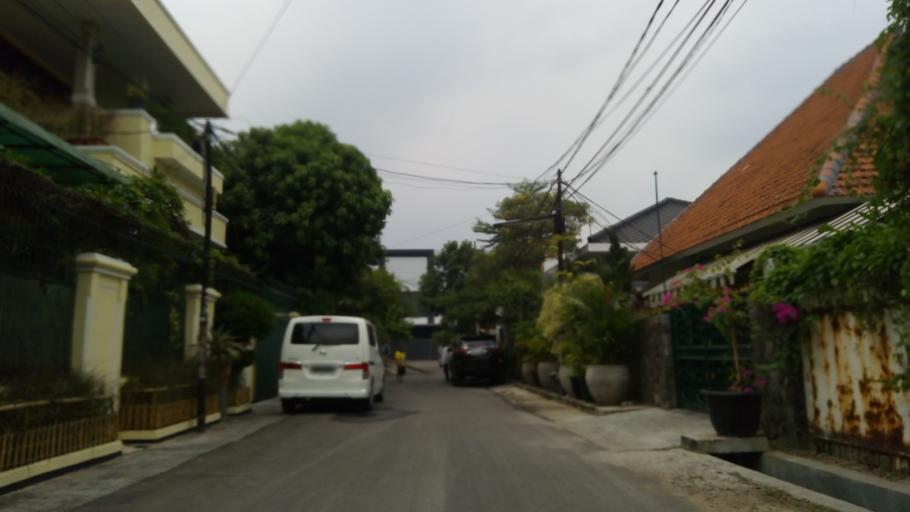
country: ID
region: Jakarta Raya
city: Jakarta
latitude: -6.1562
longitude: 106.8393
